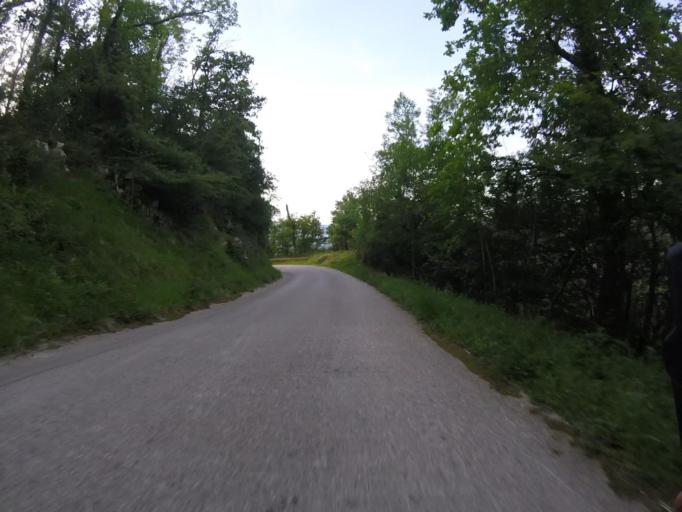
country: ES
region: Basque Country
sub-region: Provincia de Guipuzcoa
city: Errenteria
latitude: 43.2649
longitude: -1.8913
